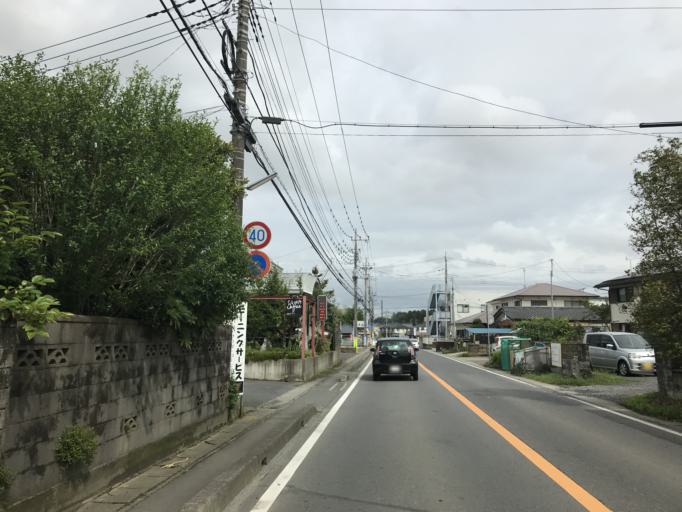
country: JP
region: Ibaraki
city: Mito-shi
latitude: 36.3245
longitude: 140.4519
